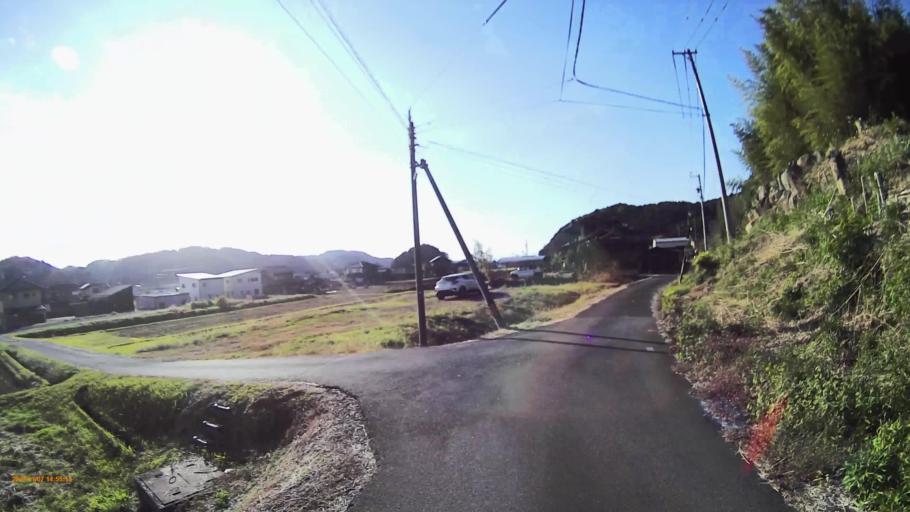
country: JP
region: Gifu
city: Mitake
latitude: 35.4291
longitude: 137.1551
